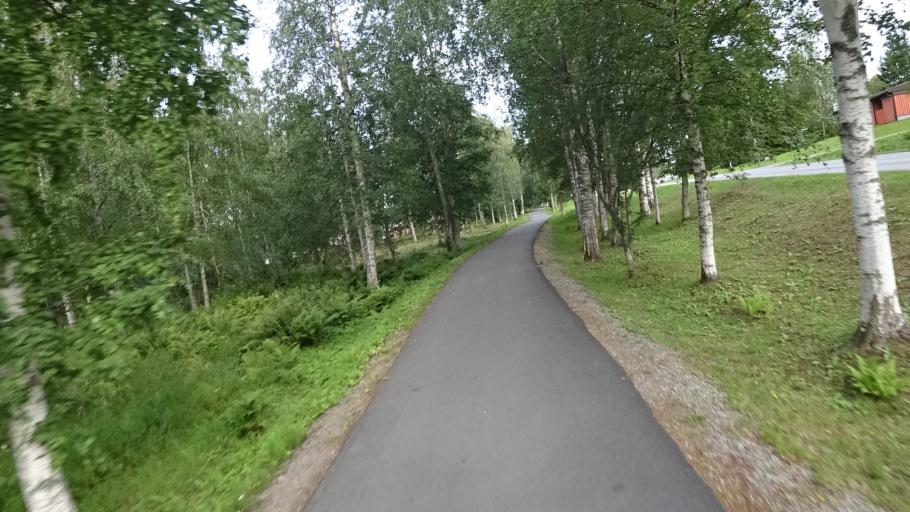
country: FI
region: North Karelia
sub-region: Joensuu
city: Ilomantsi
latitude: 62.6742
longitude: 30.9224
